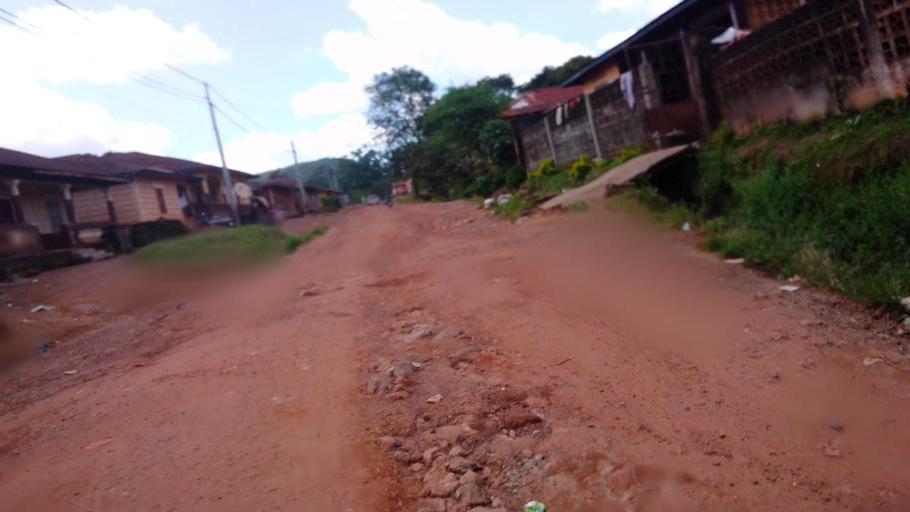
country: SL
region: Northern Province
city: Makeni
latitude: 8.8895
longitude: -12.0377
